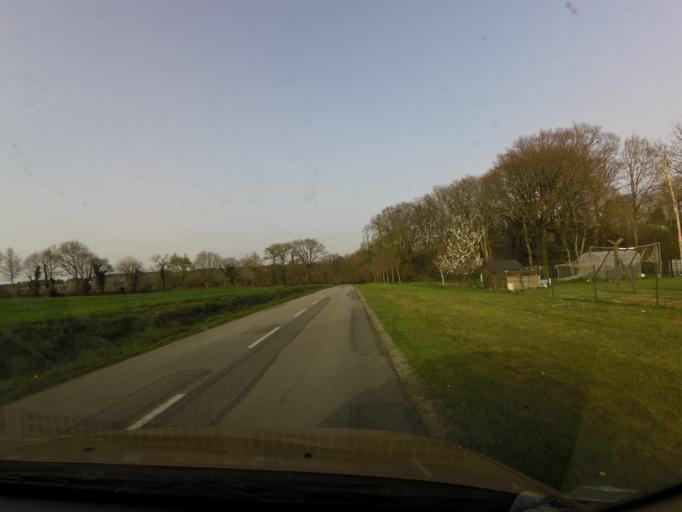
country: FR
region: Brittany
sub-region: Departement du Morbihan
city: Sulniac
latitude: 47.6781
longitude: -2.5735
